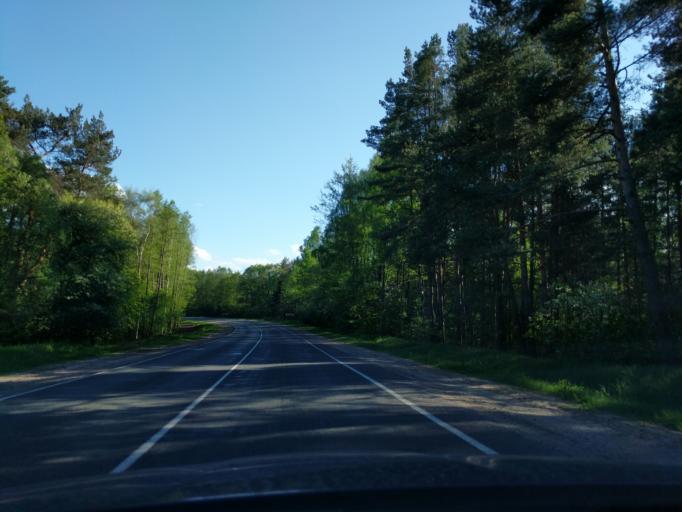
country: BY
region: Minsk
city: Myadzyel
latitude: 54.8450
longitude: 26.9260
